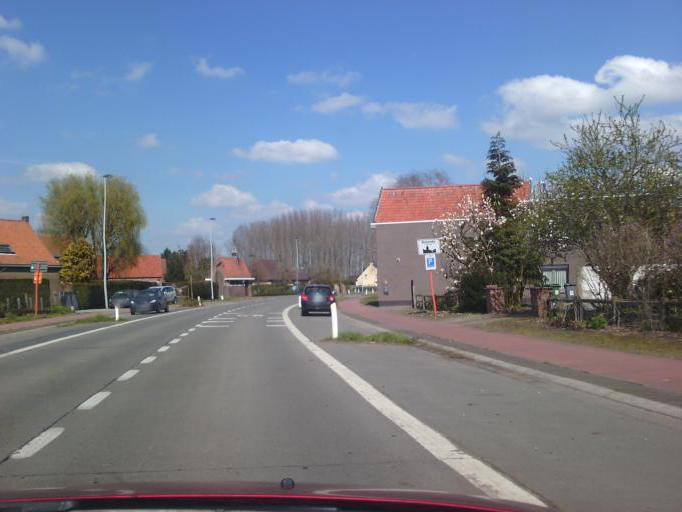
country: BE
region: Flanders
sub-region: Provincie Oost-Vlaanderen
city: Lokeren
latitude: 51.0824
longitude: 3.9507
